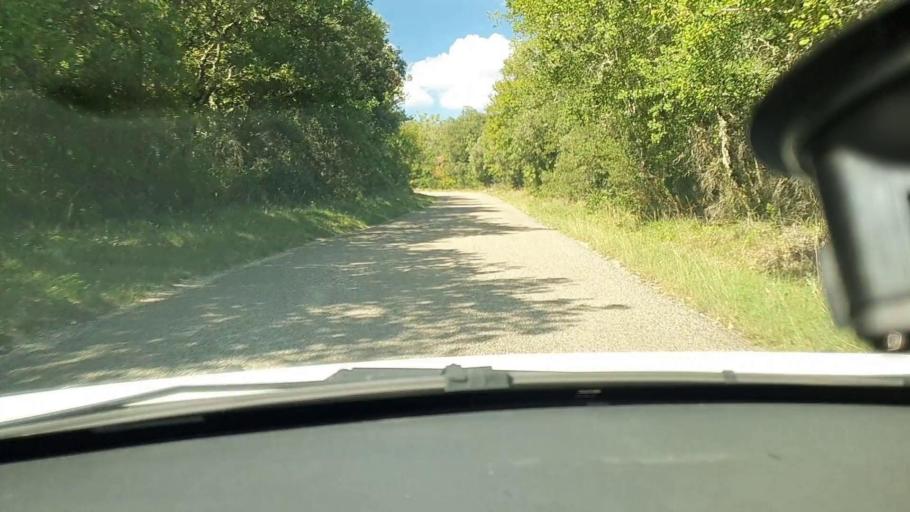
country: FR
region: Languedoc-Roussillon
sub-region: Departement du Gard
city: Goudargues
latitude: 44.1577
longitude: 4.4137
